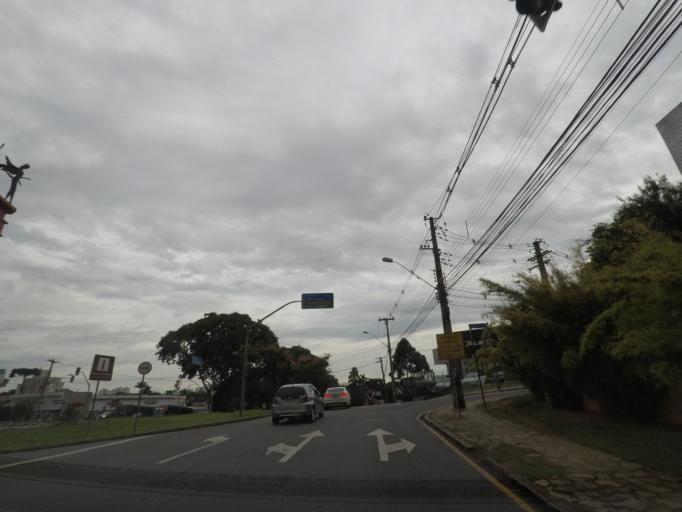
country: BR
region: Parana
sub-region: Curitiba
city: Curitiba
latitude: -25.4520
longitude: -49.3048
